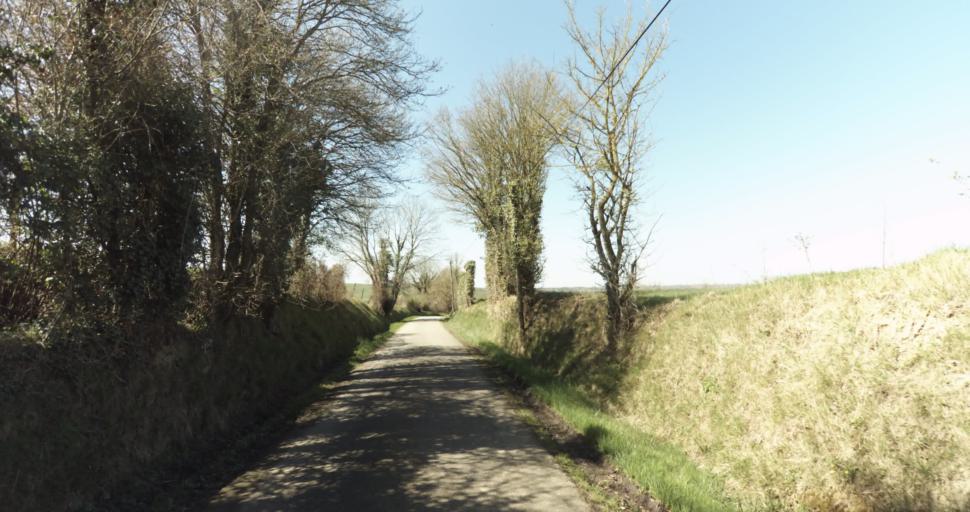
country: FR
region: Lower Normandy
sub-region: Departement du Calvados
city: Saint-Pierre-sur-Dives
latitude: 48.9889
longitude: 0.0369
